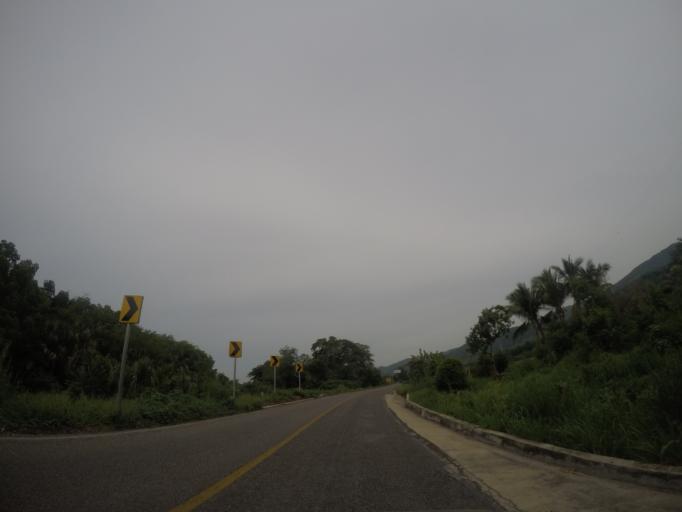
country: MX
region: Oaxaca
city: San Pedro Mixtepec
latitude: 15.9517
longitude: -97.1947
